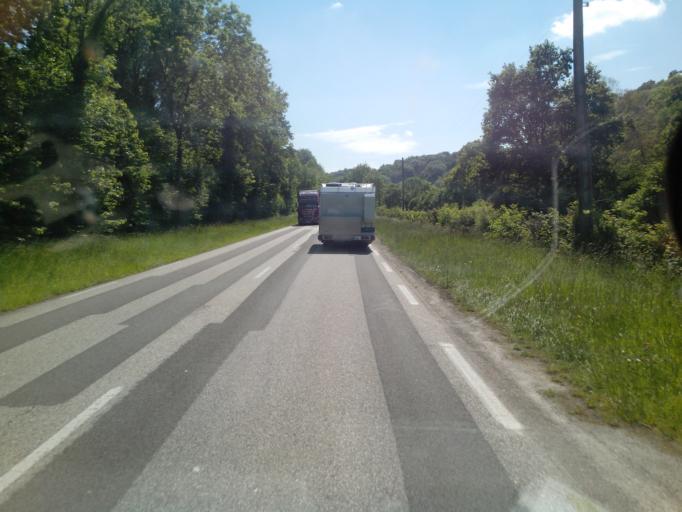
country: FR
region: Haute-Normandie
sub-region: Departement de l'Eure
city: Toutainville
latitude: 49.3955
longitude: 0.4169
